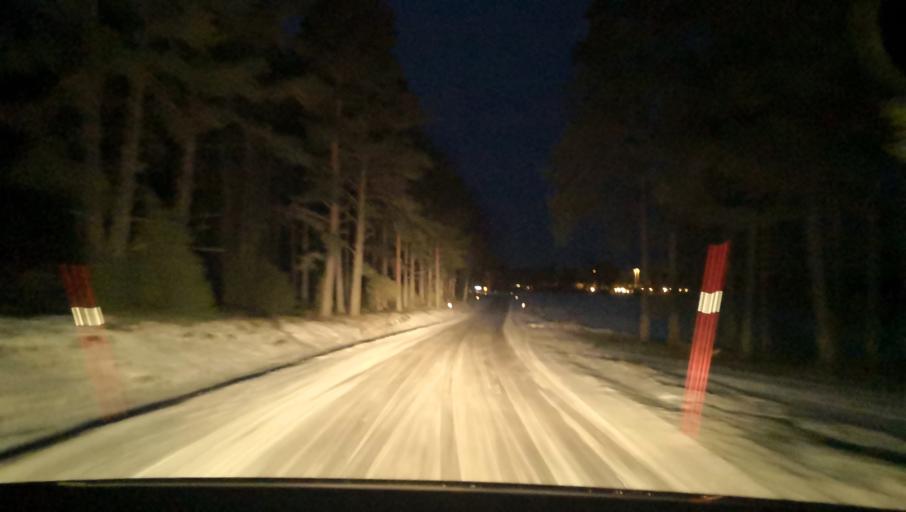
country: SE
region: Uppsala
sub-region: Heby Kommun
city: Tarnsjo
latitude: 60.2954
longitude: 16.8047
